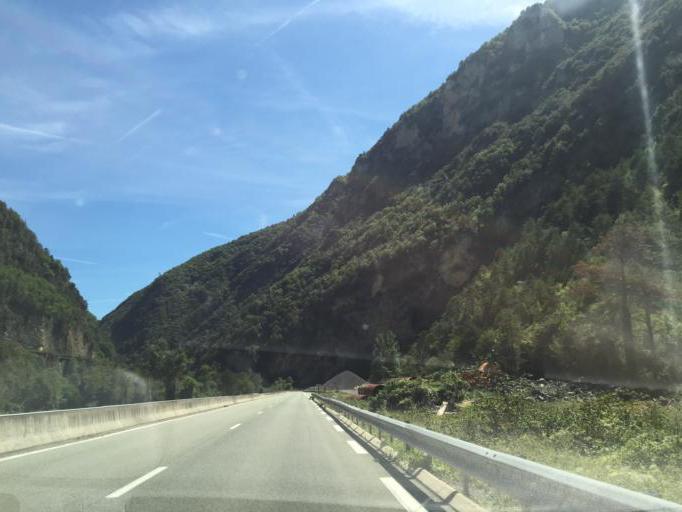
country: FR
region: Provence-Alpes-Cote d'Azur
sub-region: Departement des Alpes-Maritimes
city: Saint-Martin-Vesubie
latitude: 44.0185
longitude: 7.1315
